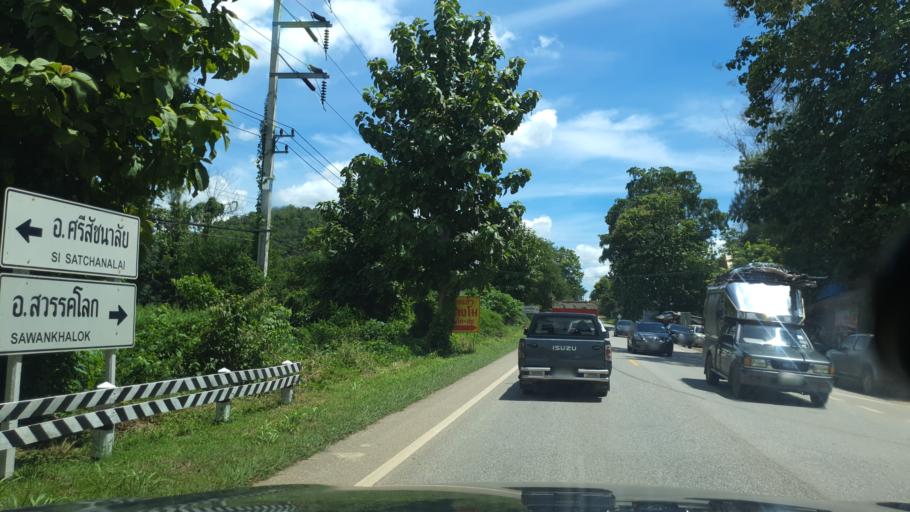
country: TH
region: Sukhothai
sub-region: Amphoe Si Satchanalai
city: Si Satchanalai
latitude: 17.4413
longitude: 99.7959
